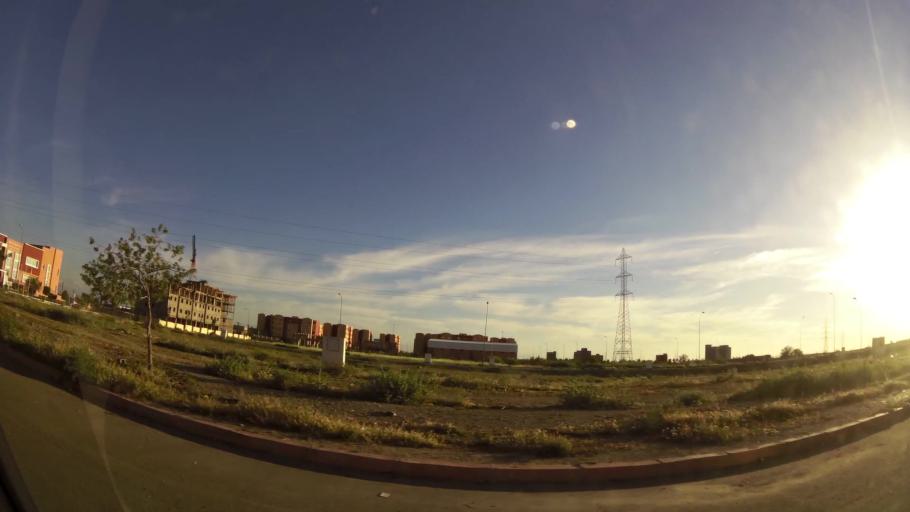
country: MA
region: Marrakech-Tensift-Al Haouz
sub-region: Marrakech
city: Marrakesh
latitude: 31.7441
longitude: -8.1252
